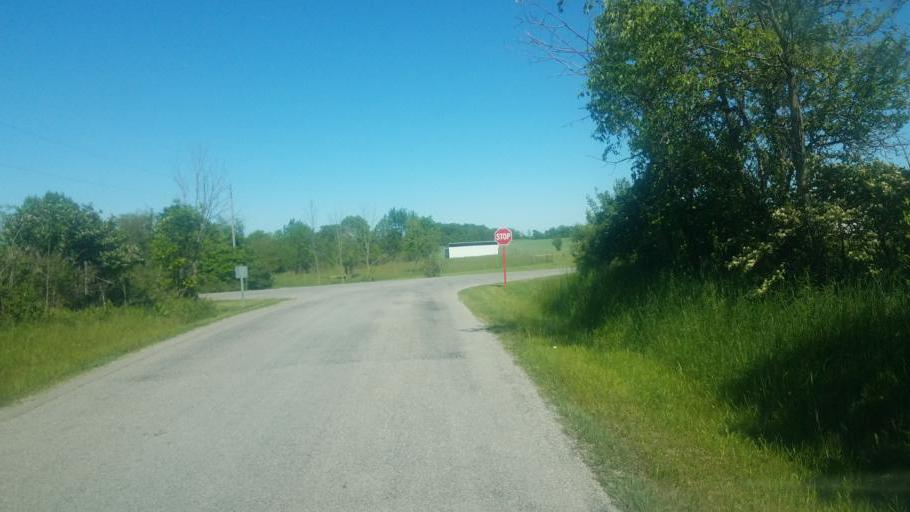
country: US
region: Ohio
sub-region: Logan County
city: Northwood
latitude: 40.4380
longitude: -83.7172
